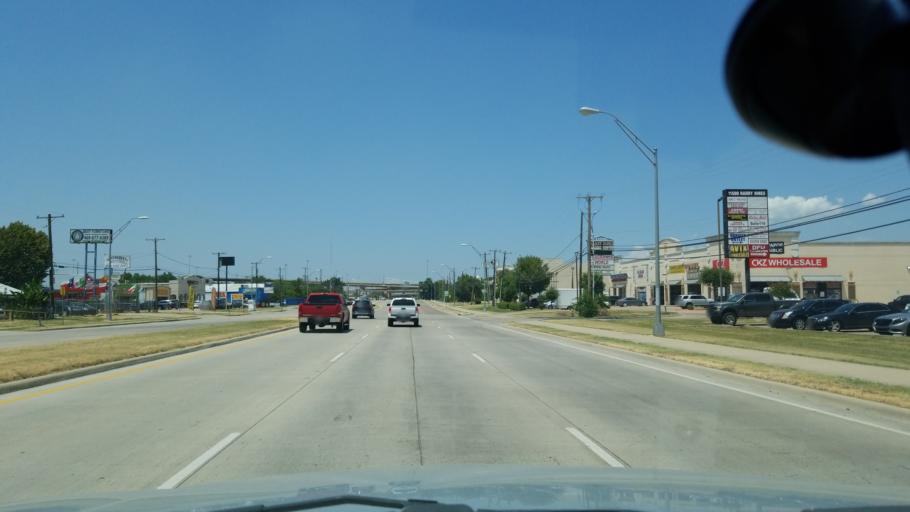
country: US
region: Texas
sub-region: Dallas County
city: Farmers Branch
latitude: 32.8993
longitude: -96.8924
